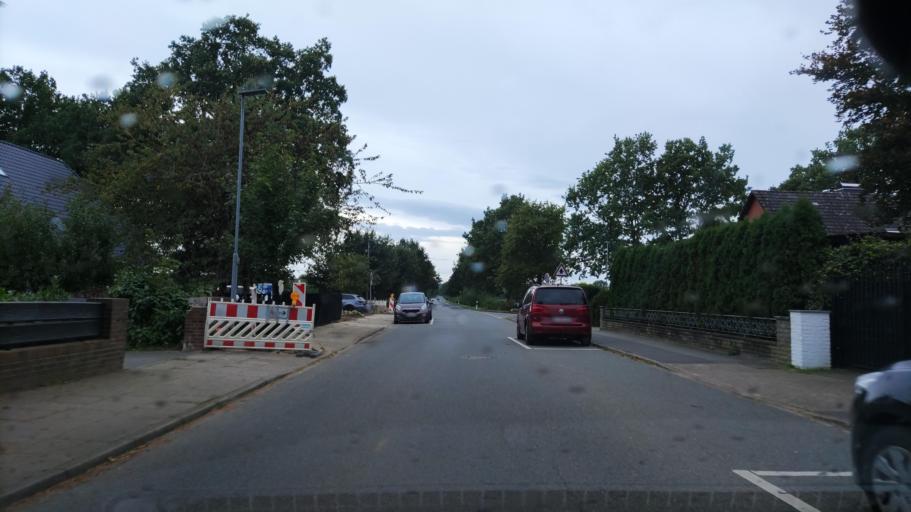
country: DE
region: Schleswig-Holstein
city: Grande
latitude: 53.5829
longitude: 10.3825
